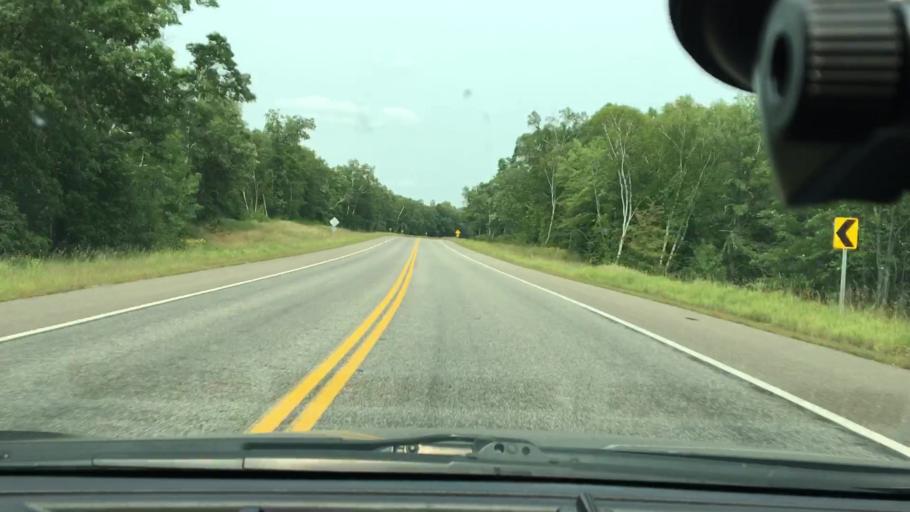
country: US
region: Minnesota
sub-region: Crow Wing County
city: Cross Lake
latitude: 46.6971
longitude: -94.0667
